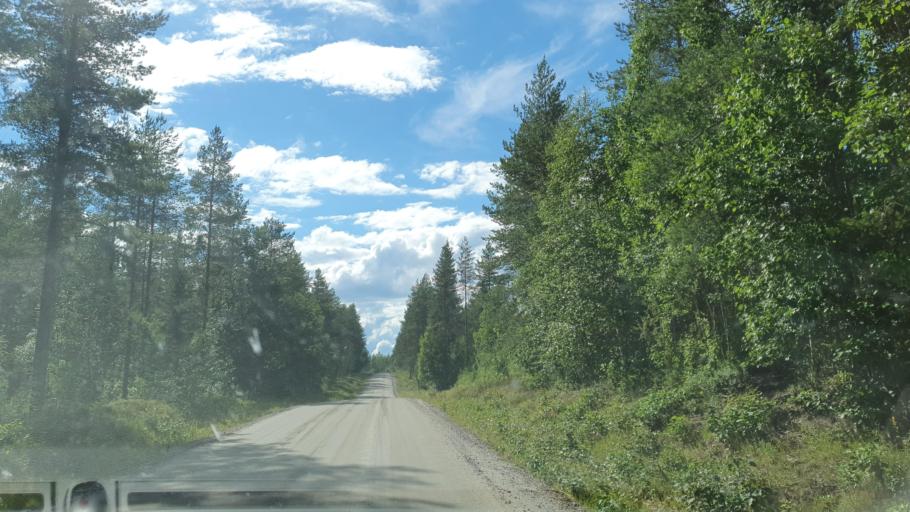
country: FI
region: Kainuu
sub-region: Kehys-Kainuu
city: Kuhmo
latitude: 64.1399
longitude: 29.6945
